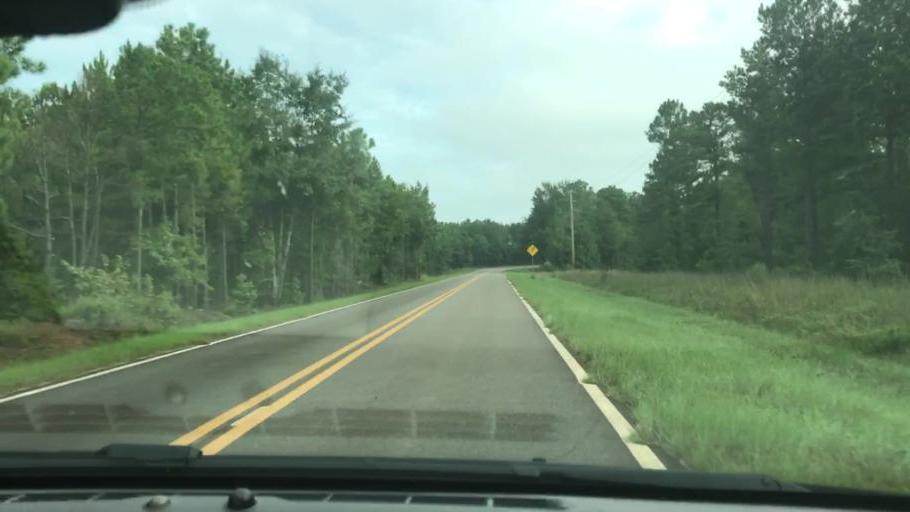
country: US
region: Georgia
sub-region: Stewart County
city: Lumpkin
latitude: 32.0402
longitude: -84.9094
